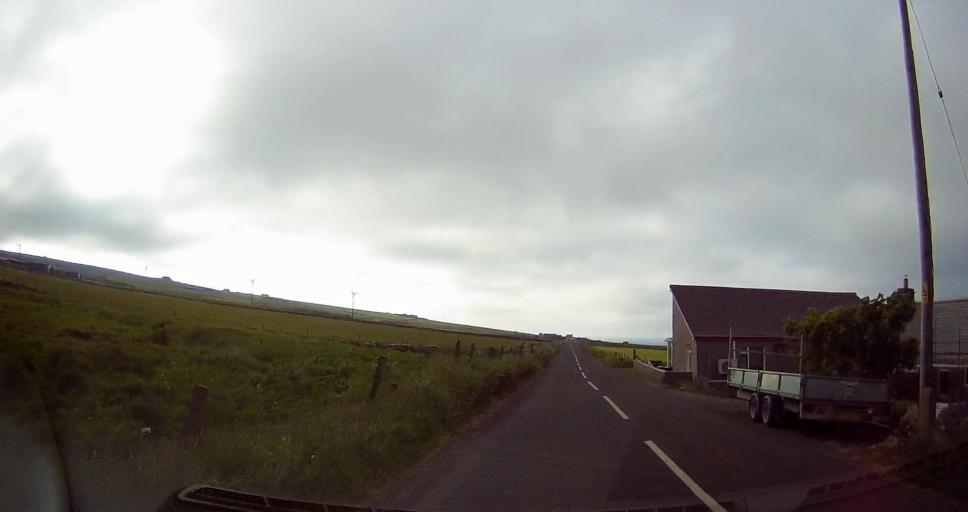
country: GB
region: Scotland
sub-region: Orkney Islands
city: Orkney
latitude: 59.1182
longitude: -3.1188
